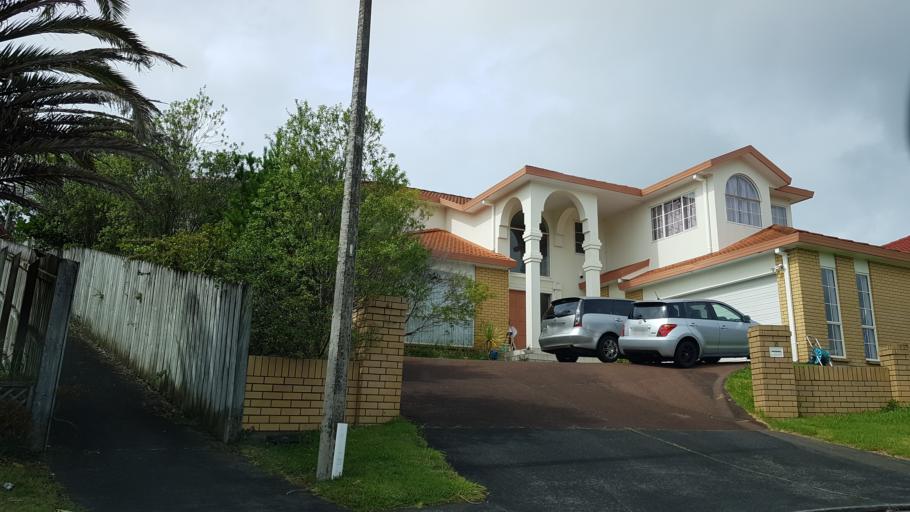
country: NZ
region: Auckland
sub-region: Auckland
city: North Shore
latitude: -36.7878
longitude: 174.7354
